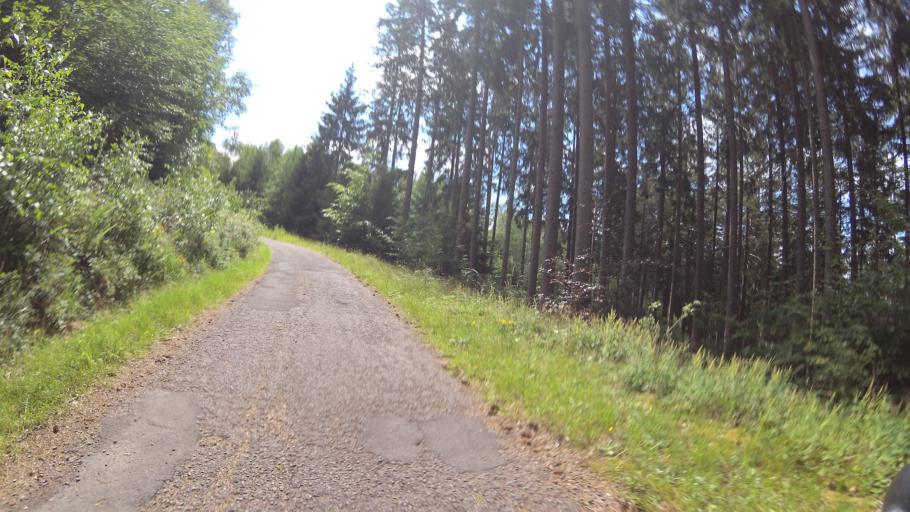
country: DE
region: Saarland
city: Weiskirchen
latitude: 49.5587
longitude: 6.7813
